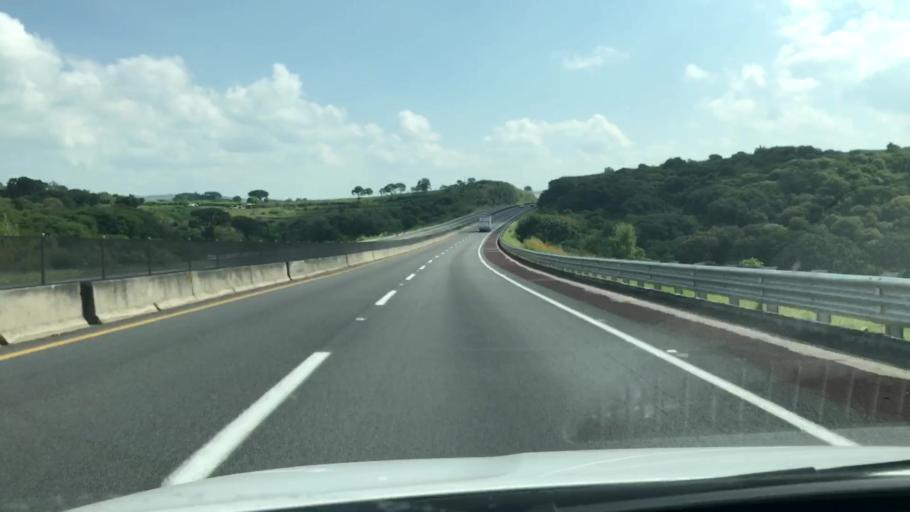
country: MX
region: Jalisco
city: Zapotlanejo
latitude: 20.6632
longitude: -103.0460
